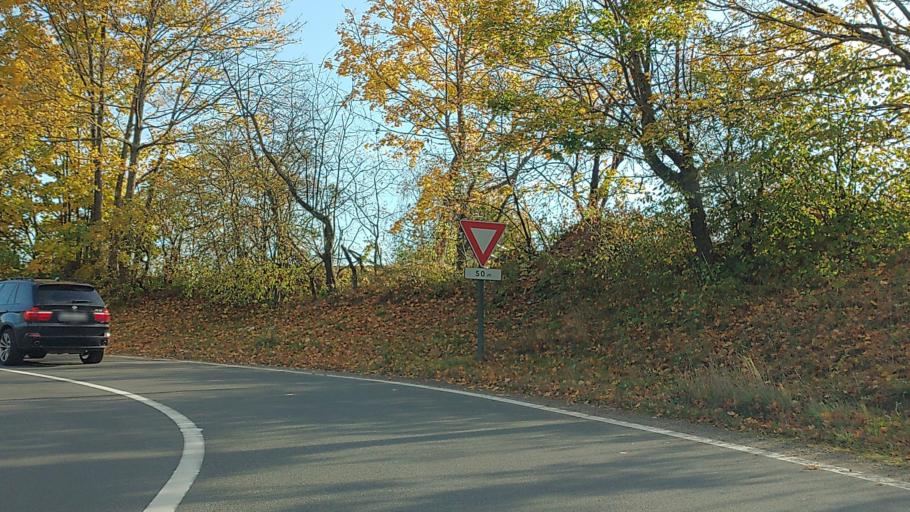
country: FR
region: Ile-de-France
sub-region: Departement du Val-d'Oise
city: Survilliers
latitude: 49.0913
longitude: 2.5295
